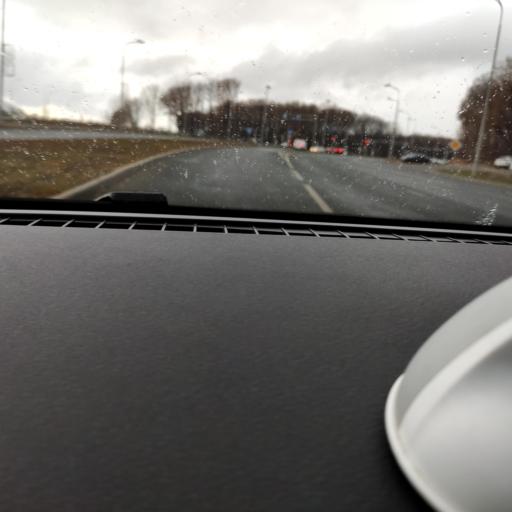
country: RU
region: Samara
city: Petra-Dubrava
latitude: 53.2782
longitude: 50.2557
